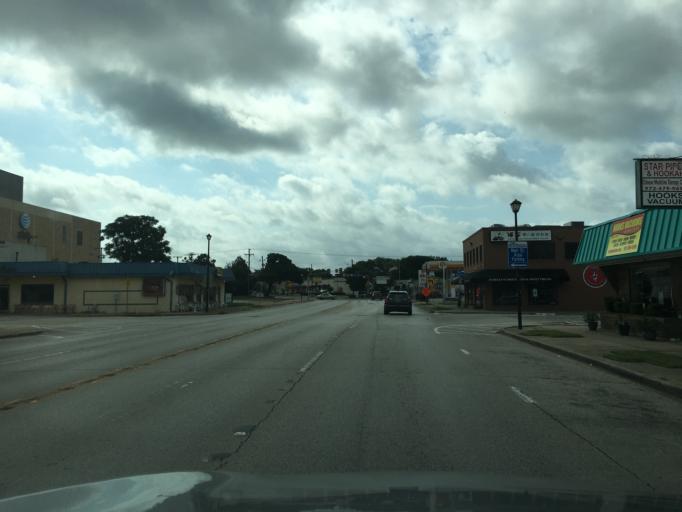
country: US
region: Texas
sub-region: Dallas County
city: Richardson
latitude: 32.9489
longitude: -96.7312
